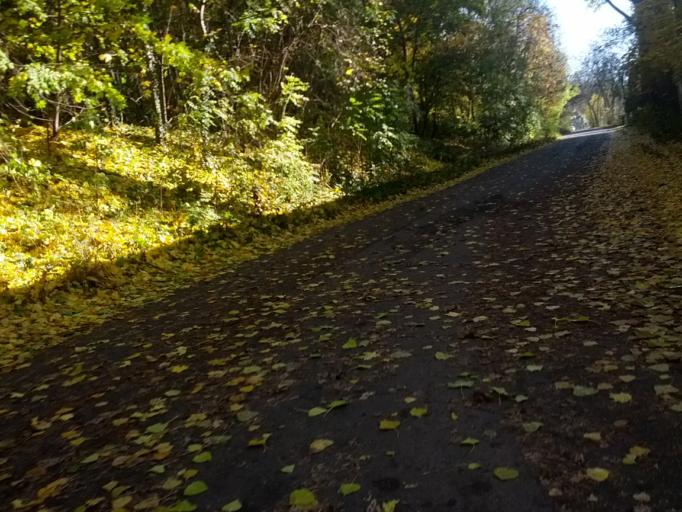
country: DE
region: Thuringia
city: Gotha
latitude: 50.9644
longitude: 10.7033
